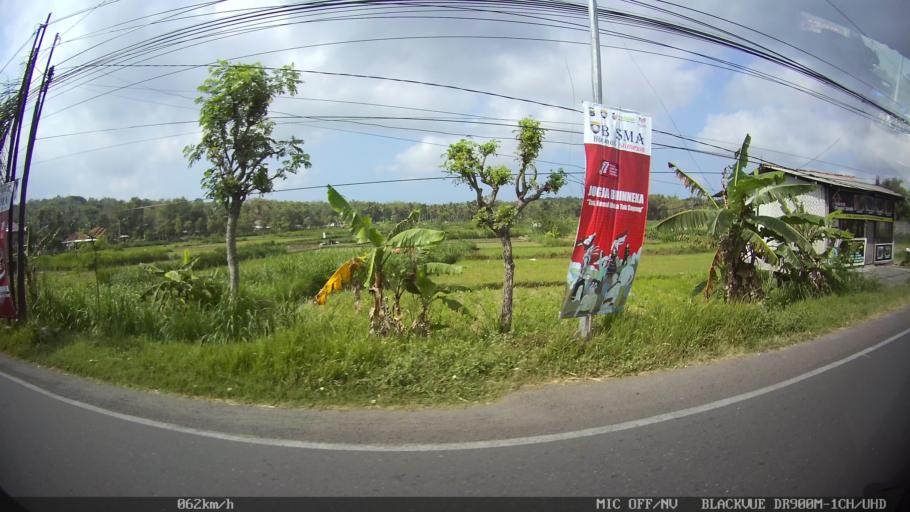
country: ID
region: Daerah Istimewa Yogyakarta
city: Srandakan
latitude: -7.8669
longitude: 110.1758
